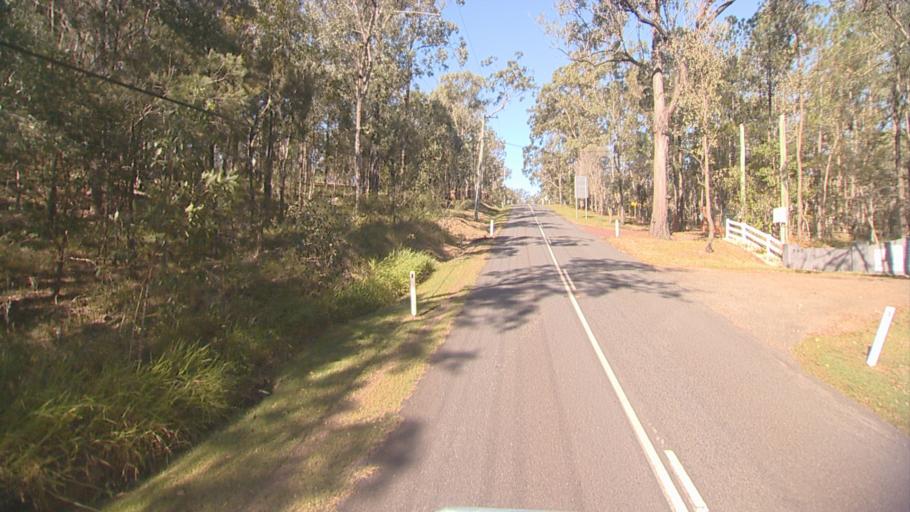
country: AU
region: Queensland
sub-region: Logan
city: Springwood
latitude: -27.6019
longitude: 153.1692
